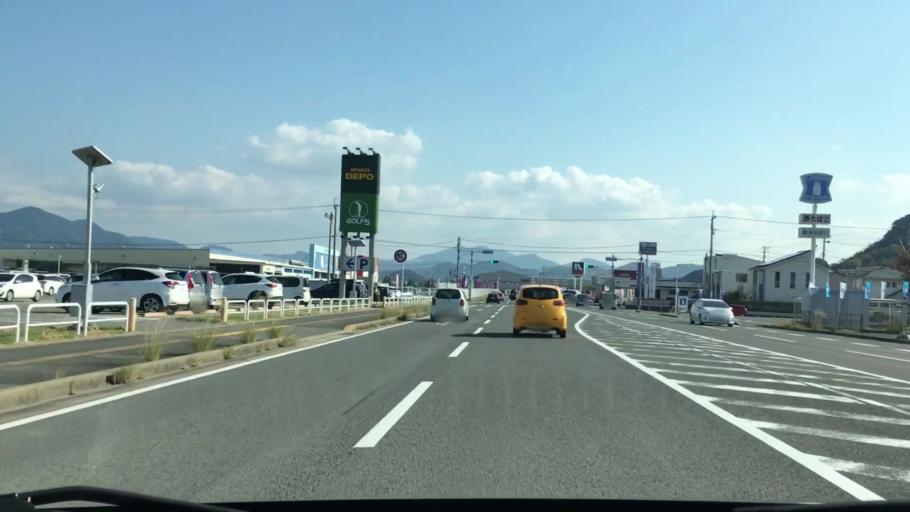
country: JP
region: Nagasaki
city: Togitsu
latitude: 32.8506
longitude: 129.8278
